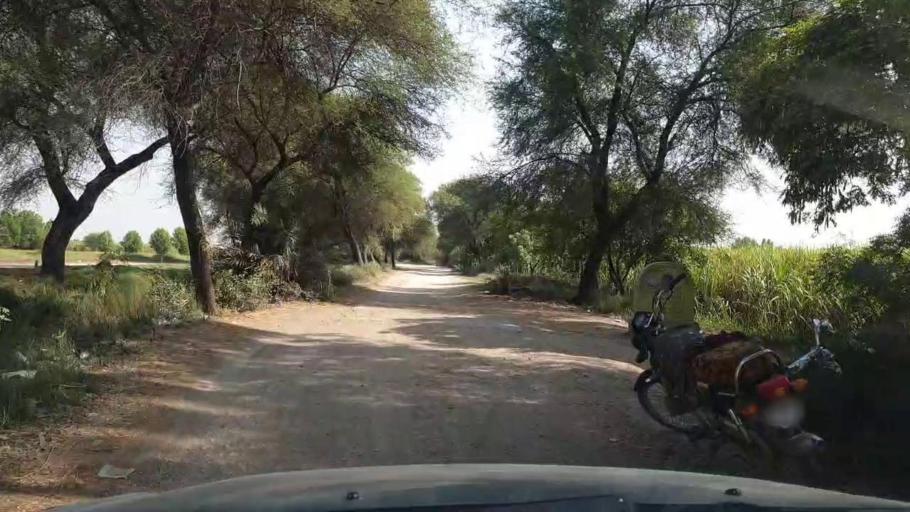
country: PK
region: Sindh
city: Bulri
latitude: 24.9052
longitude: 68.3750
